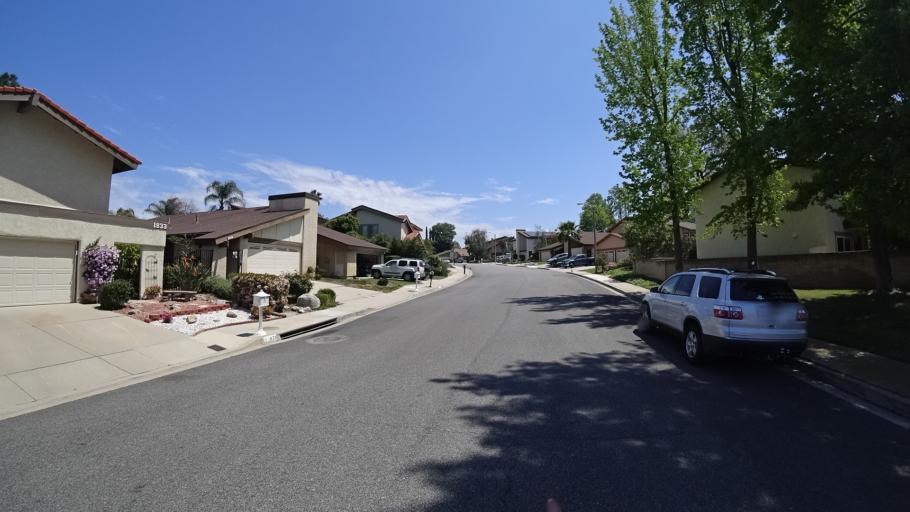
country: US
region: California
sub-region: Ventura County
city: Casa Conejo
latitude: 34.1809
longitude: -118.9192
